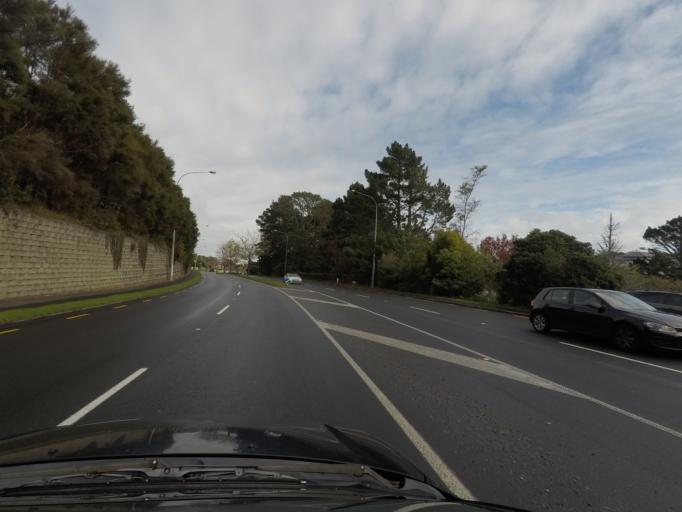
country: NZ
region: Auckland
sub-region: Auckland
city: Rothesay Bay
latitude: -36.7110
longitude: 174.7238
